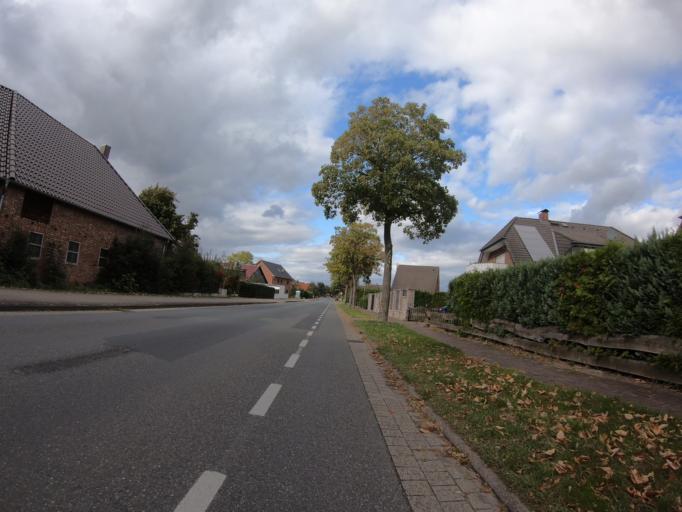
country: DE
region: Lower Saxony
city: Isenbuttel
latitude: 52.4283
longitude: 10.5858
